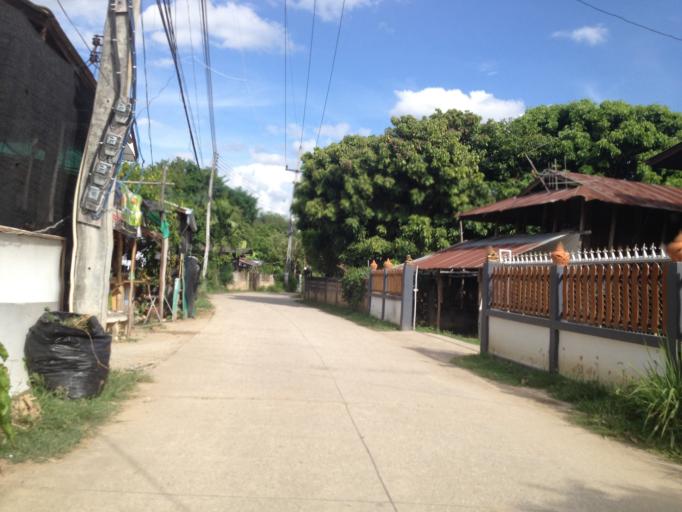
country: TH
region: Chiang Mai
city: Hang Dong
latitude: 18.7116
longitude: 98.9229
